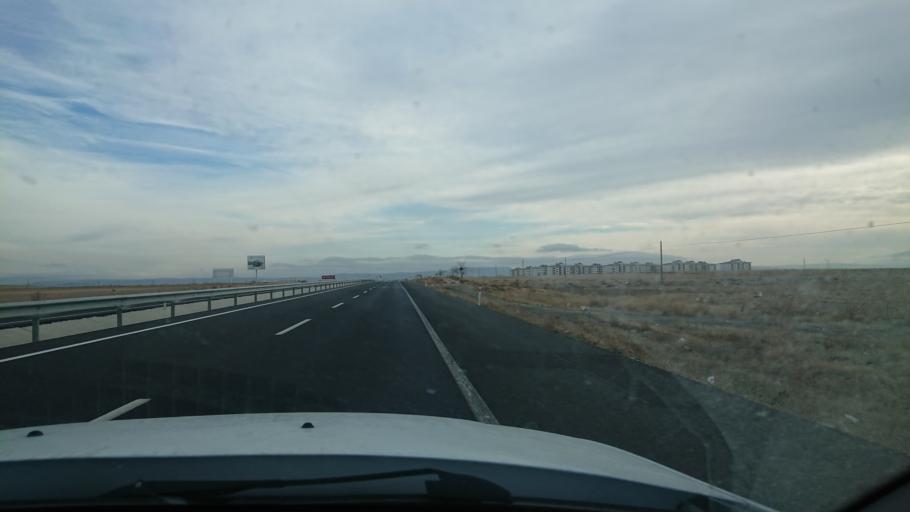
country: TR
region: Aksaray
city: Yesilova
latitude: 38.3312
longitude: 33.9091
